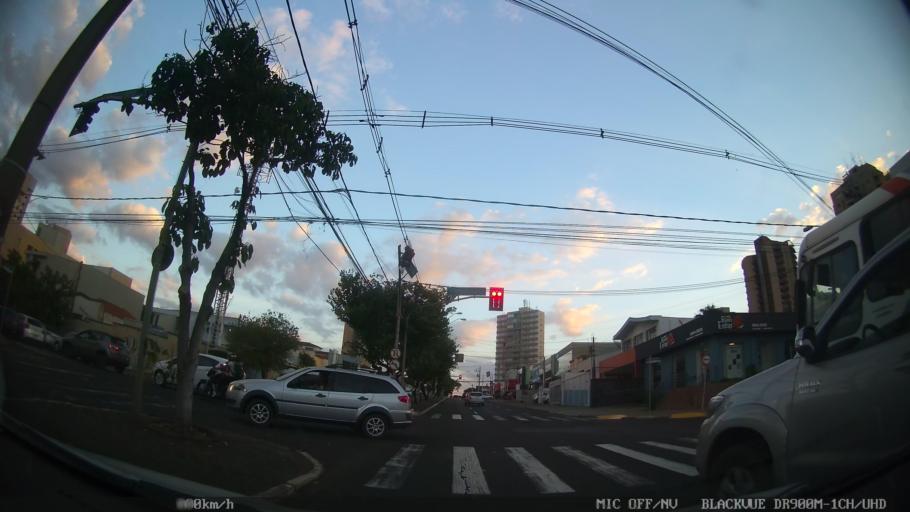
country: BR
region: Sao Paulo
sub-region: Ribeirao Preto
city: Ribeirao Preto
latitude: -21.1854
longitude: -47.8049
